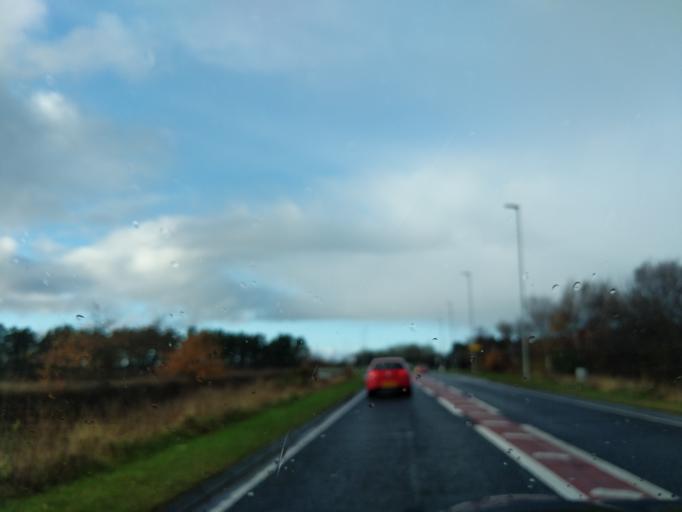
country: GB
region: England
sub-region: Northumberland
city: Seaton Delaval
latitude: 55.1036
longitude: -1.5391
